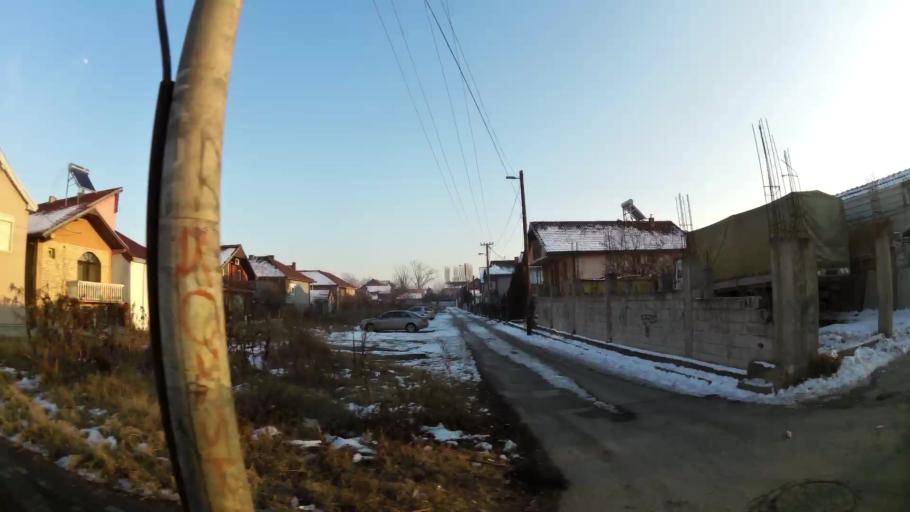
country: MK
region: Kisela Voda
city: Kisela Voda
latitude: 41.9741
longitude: 21.4881
